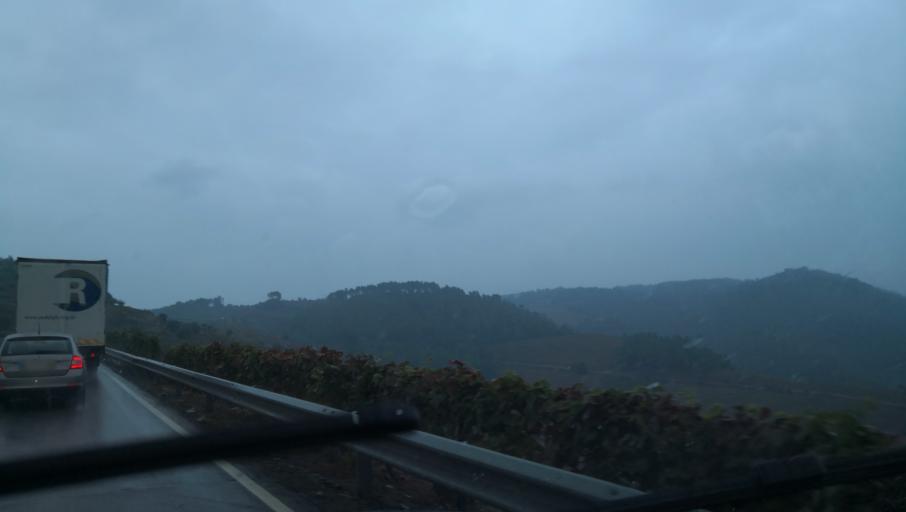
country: PT
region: Vila Real
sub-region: Vila Real
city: Vila Real
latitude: 41.2318
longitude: -7.7271
